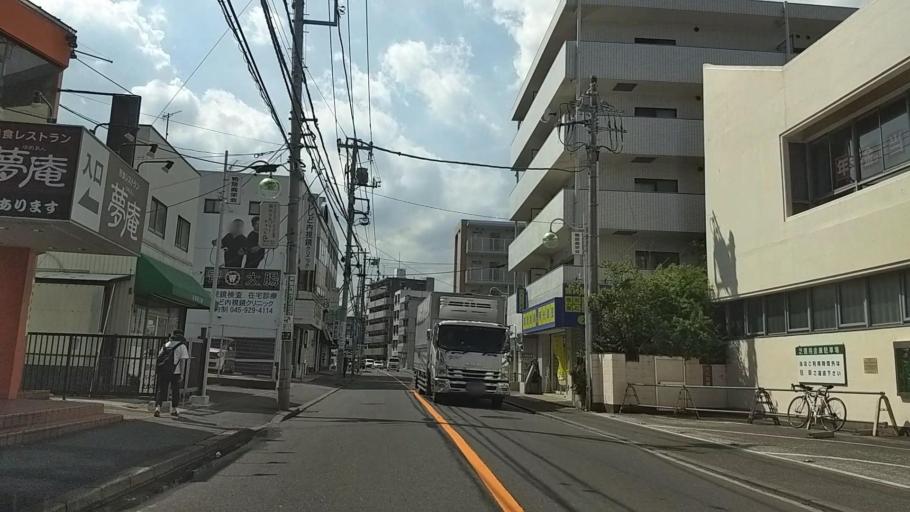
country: JP
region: Kanagawa
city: Yokohama
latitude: 35.5102
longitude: 139.5667
